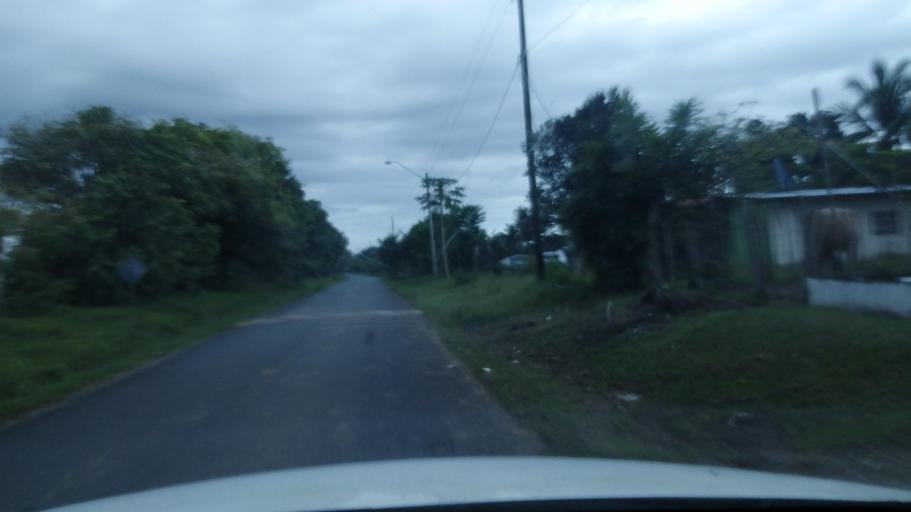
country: PA
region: Chiriqui
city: Alanje
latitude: 8.4096
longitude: -82.5017
